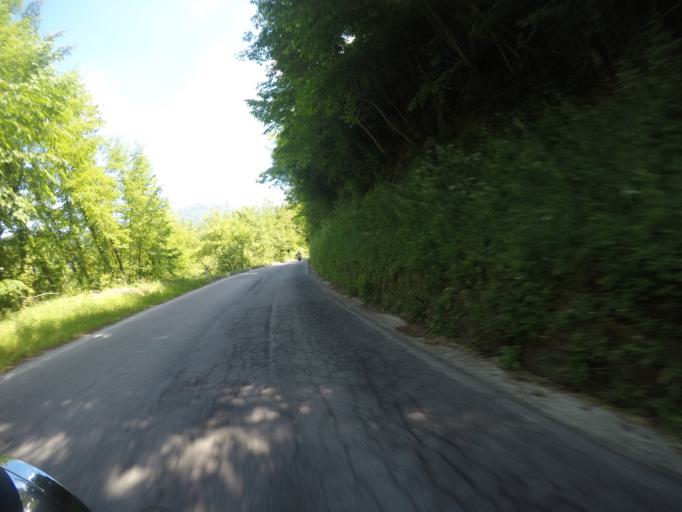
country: IT
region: Tuscany
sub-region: Provincia di Lucca
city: Camporgiano
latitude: 44.1407
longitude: 10.3479
